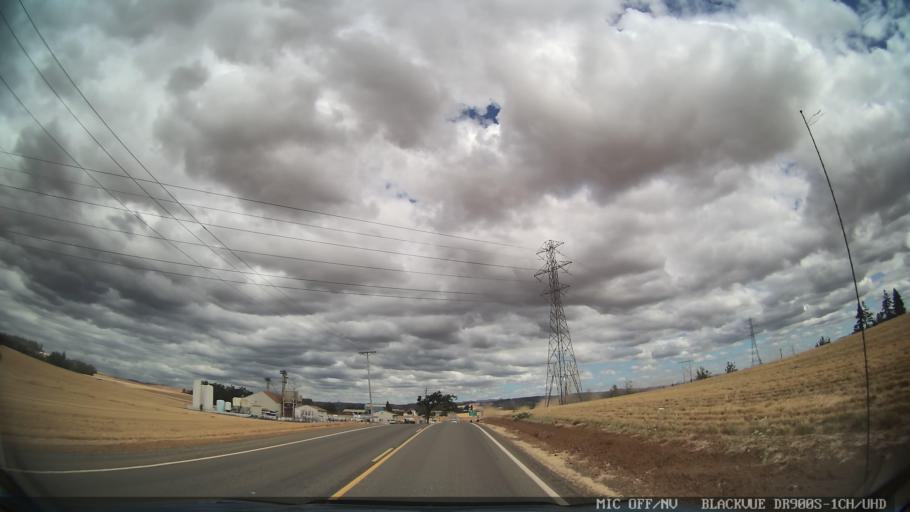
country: US
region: Oregon
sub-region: Marion County
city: Sublimity
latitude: 44.8663
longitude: -122.7940
